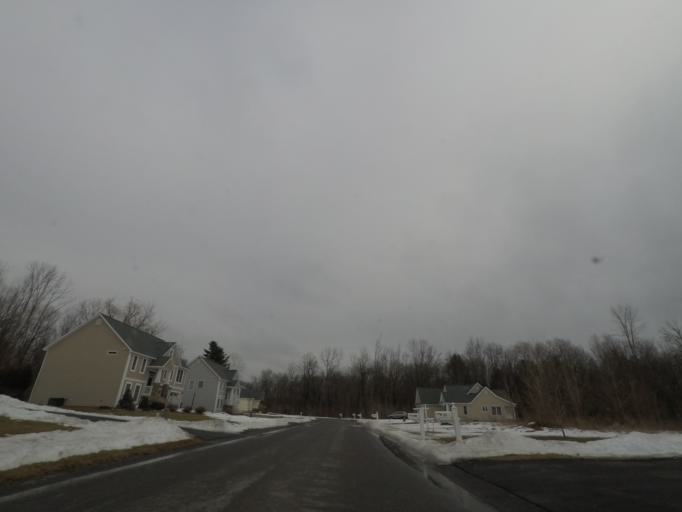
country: US
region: New York
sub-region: Schenectady County
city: Rotterdam
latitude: 42.7639
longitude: -73.9771
